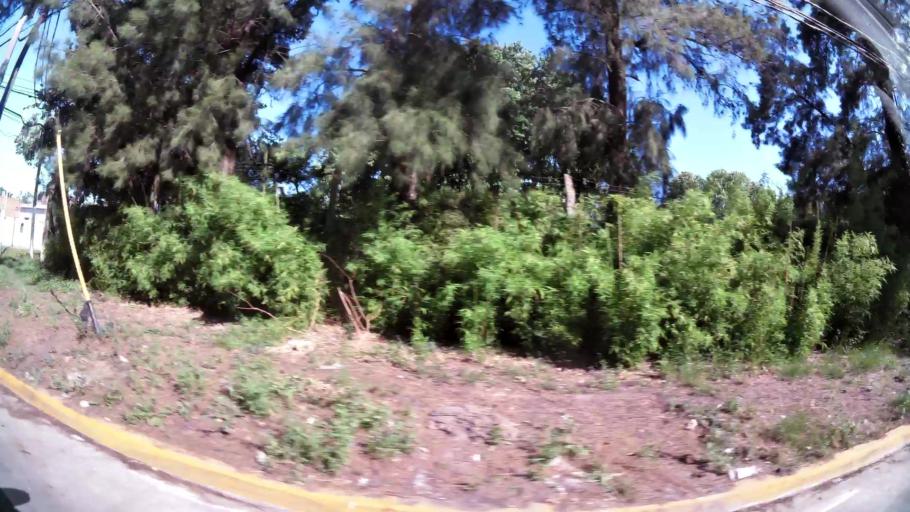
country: AR
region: Buenos Aires
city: Santa Catalina - Dique Lujan
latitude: -34.4915
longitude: -58.6938
